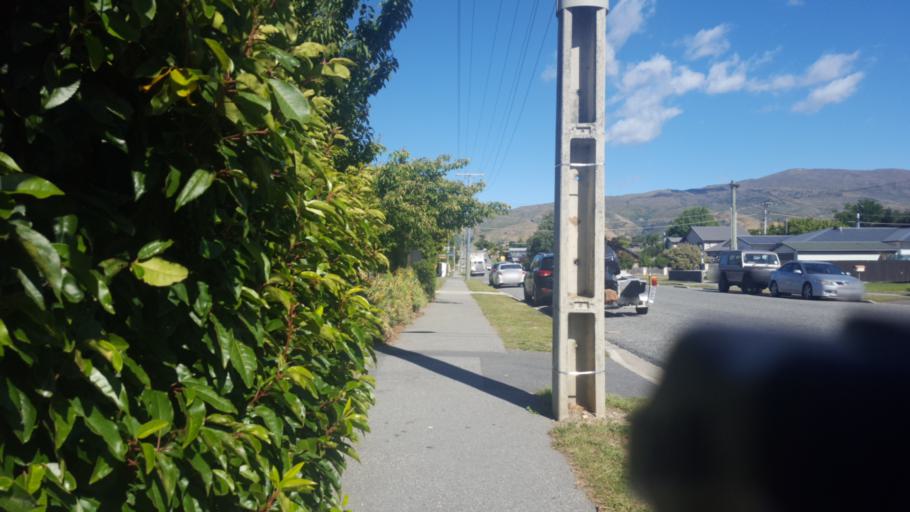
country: NZ
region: Otago
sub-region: Queenstown-Lakes District
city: Wanaka
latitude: -45.0483
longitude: 169.2066
